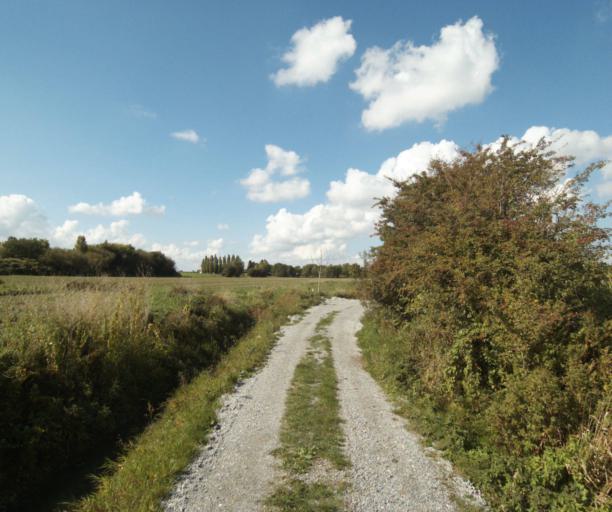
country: FR
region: Nord-Pas-de-Calais
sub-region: Departement du Nord
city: Illies
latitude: 50.5717
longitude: 2.8313
